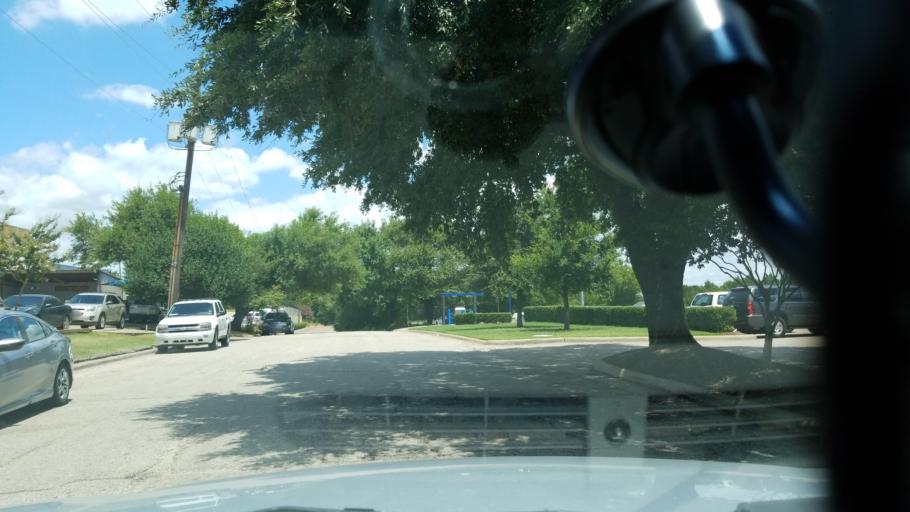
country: US
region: Texas
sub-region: Dallas County
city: Duncanville
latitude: 32.6626
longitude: -96.8784
